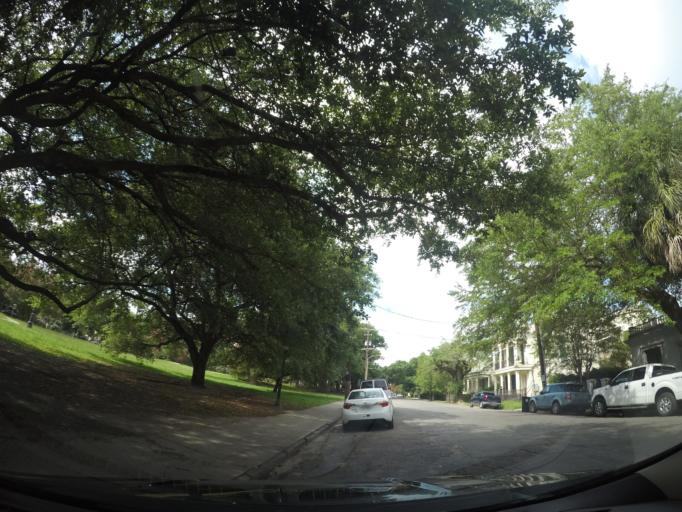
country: US
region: Louisiana
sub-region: Orleans Parish
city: New Orleans
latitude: 29.9361
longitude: -90.0738
